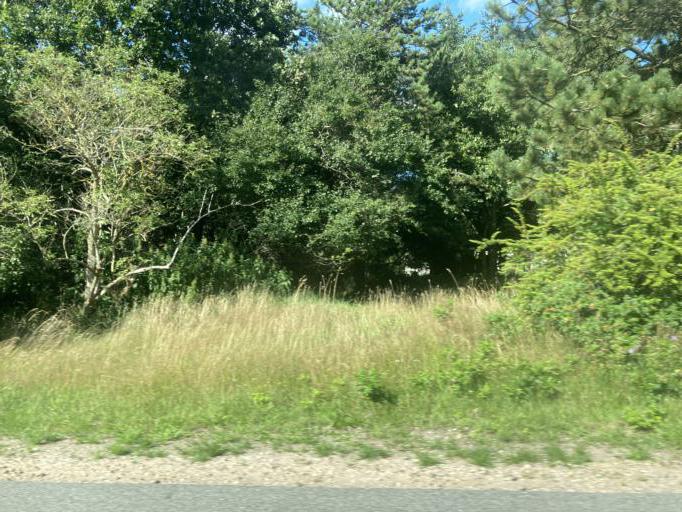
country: DK
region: South Denmark
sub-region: Esbjerg Kommune
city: Ribe
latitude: 55.2851
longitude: 8.7173
